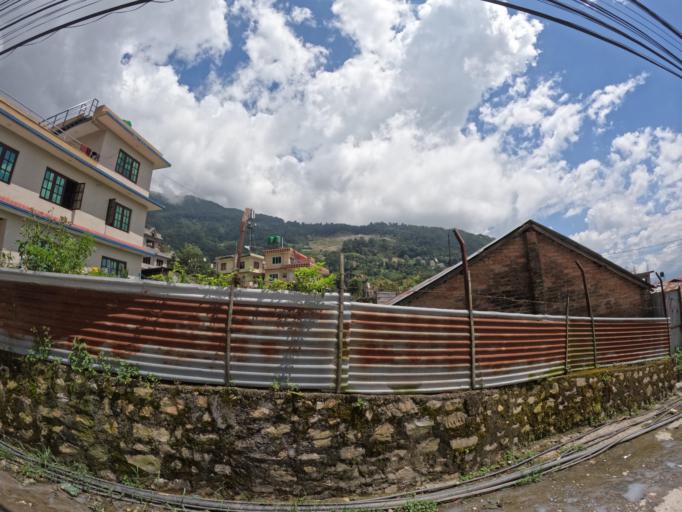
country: NP
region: Central Region
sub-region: Bagmati Zone
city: Kathmandu
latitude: 27.7955
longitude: 85.3305
